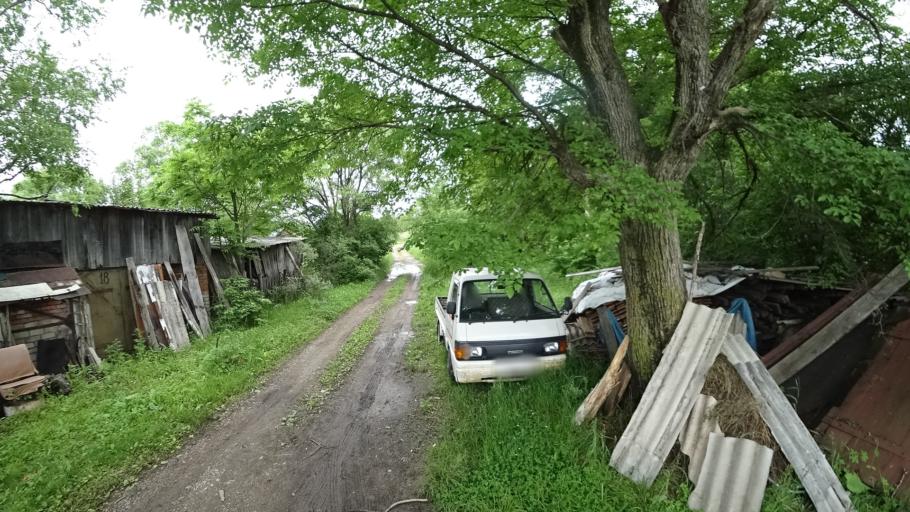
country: RU
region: Primorskiy
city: Novosysoyevka
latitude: 44.2071
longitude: 133.3258
